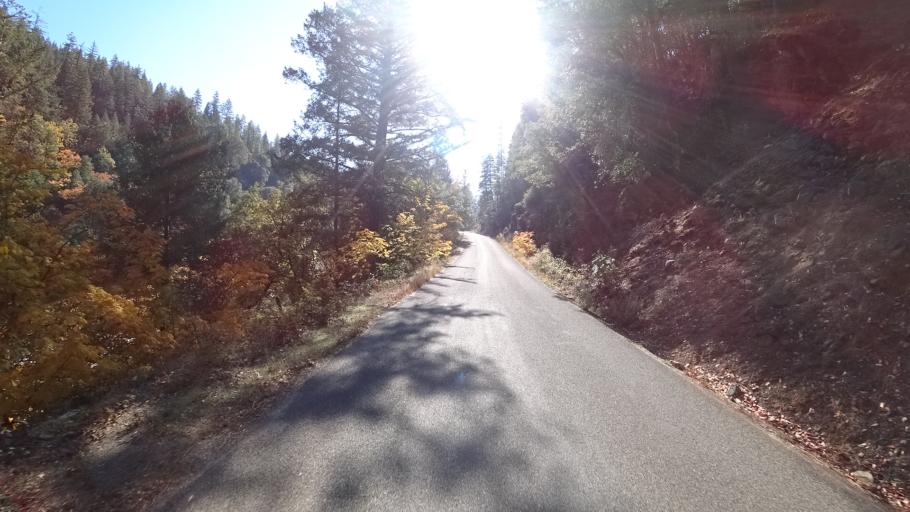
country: US
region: California
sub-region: Siskiyou County
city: Happy Camp
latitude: 41.7615
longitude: -123.0156
